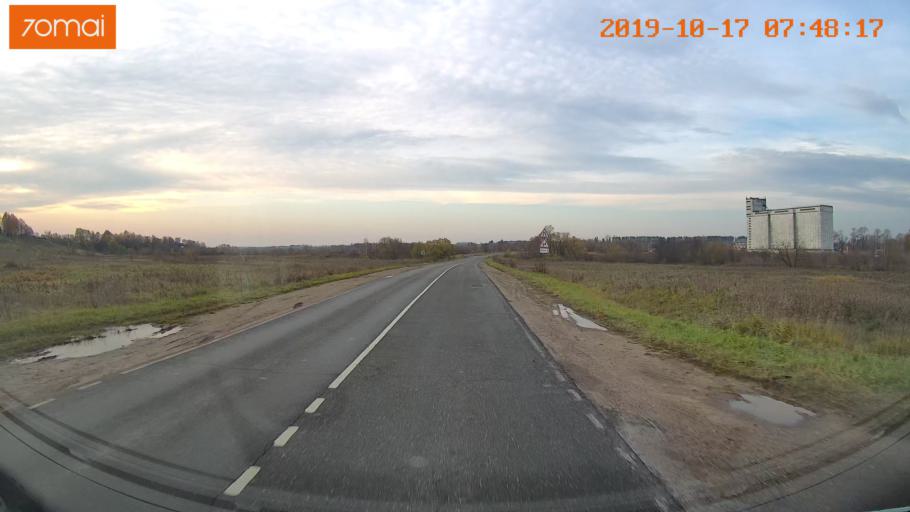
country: RU
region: Vladimir
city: Yur'yev-Pol'skiy
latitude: 56.4814
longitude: 39.6765
